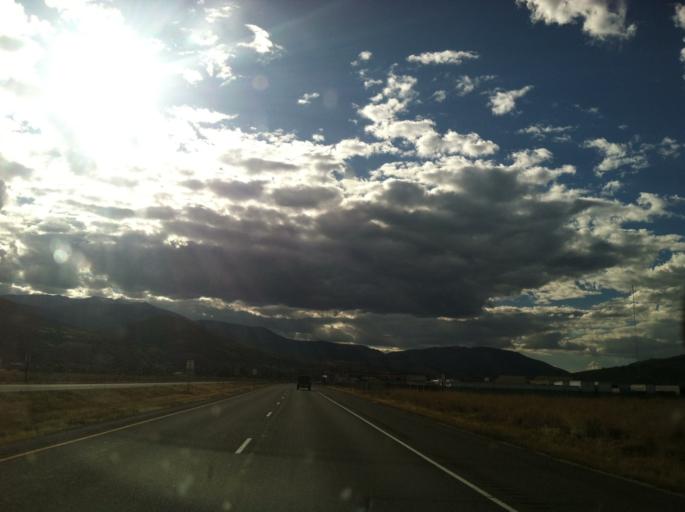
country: US
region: Montana
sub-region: Deer Lodge County
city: Anaconda
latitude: 46.1271
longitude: -112.9181
